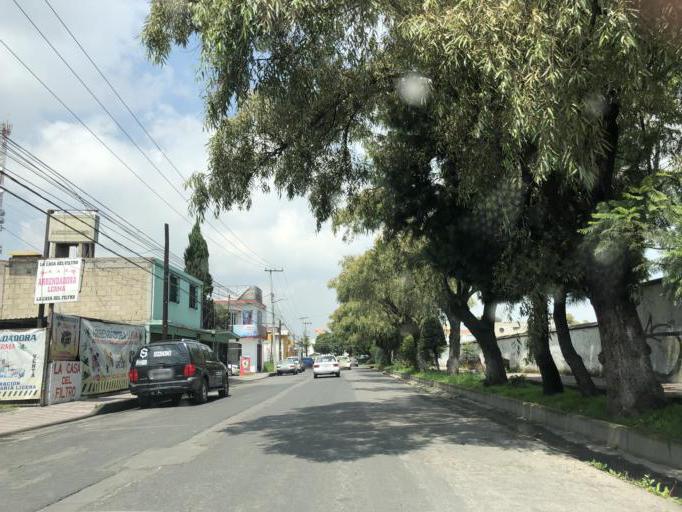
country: MX
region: Morelos
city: Lerma de Villada
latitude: 19.2869
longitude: -99.5176
